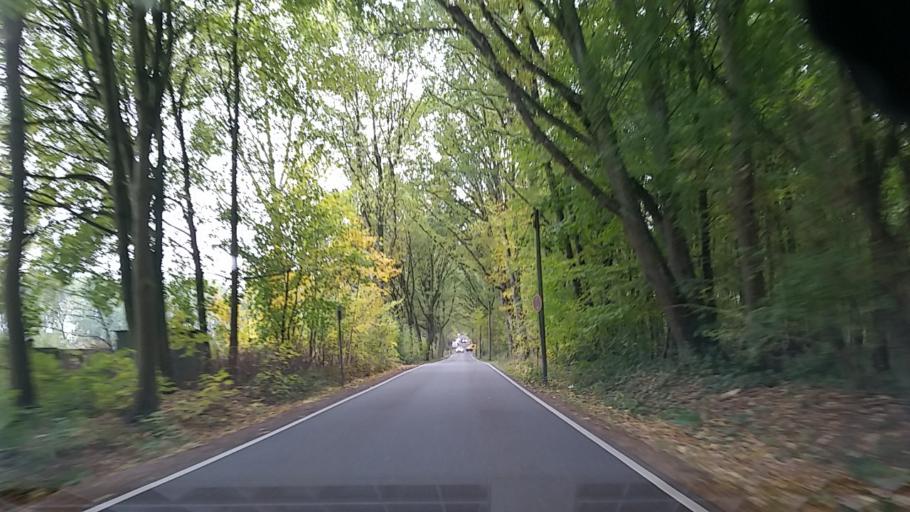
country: DE
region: Schleswig-Holstein
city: Oststeinbek
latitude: 53.5513
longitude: 10.1468
